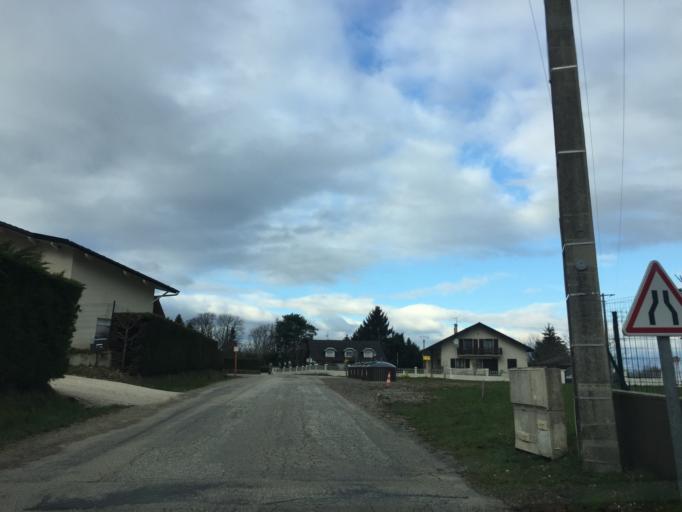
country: FR
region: Rhone-Alpes
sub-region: Departement de la Savoie
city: Vimines
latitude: 45.5455
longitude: 5.8499
